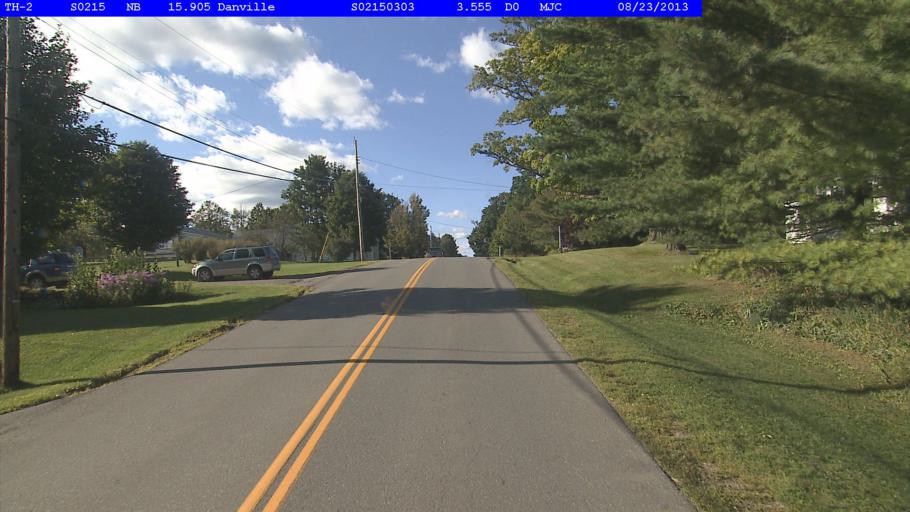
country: US
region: Vermont
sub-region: Caledonia County
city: Saint Johnsbury
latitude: 44.4153
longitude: -72.1413
